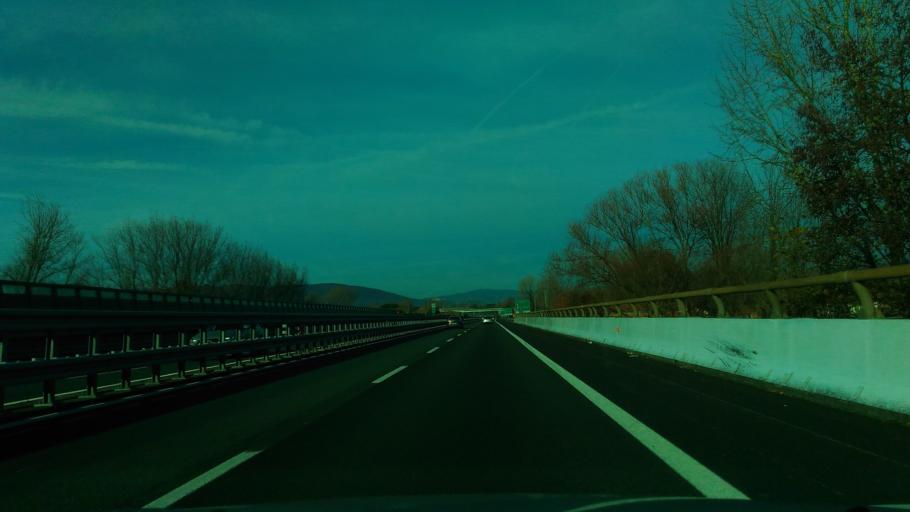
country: IT
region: Tuscany
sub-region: Provincia di Massa-Carrara
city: Marina di Carrara
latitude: 44.0480
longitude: 10.0434
